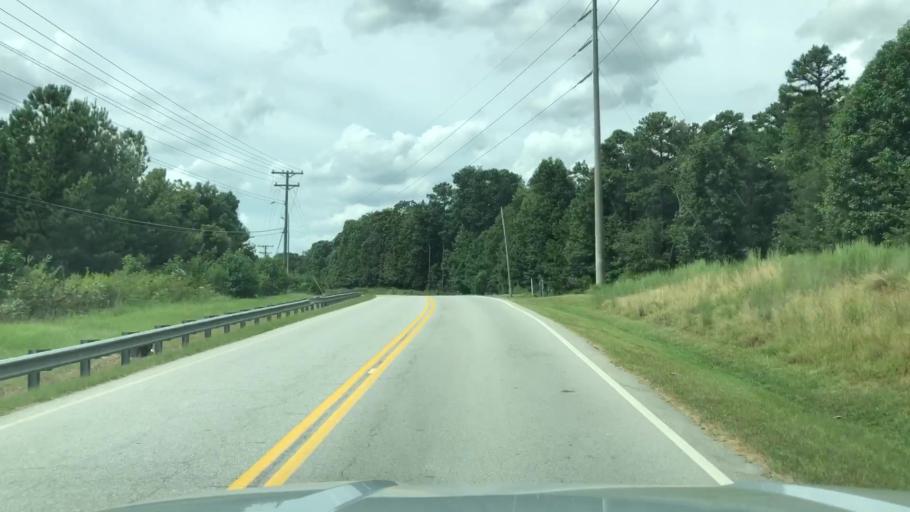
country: US
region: Georgia
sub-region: Gwinnett County
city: Suwanee
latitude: 34.0359
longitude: -84.0358
